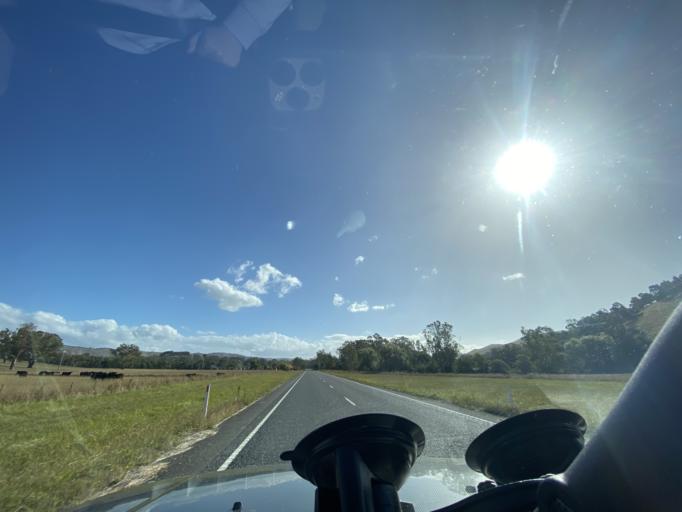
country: AU
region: Victoria
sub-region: Murrindindi
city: Kinglake West
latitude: -37.2472
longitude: 145.3851
